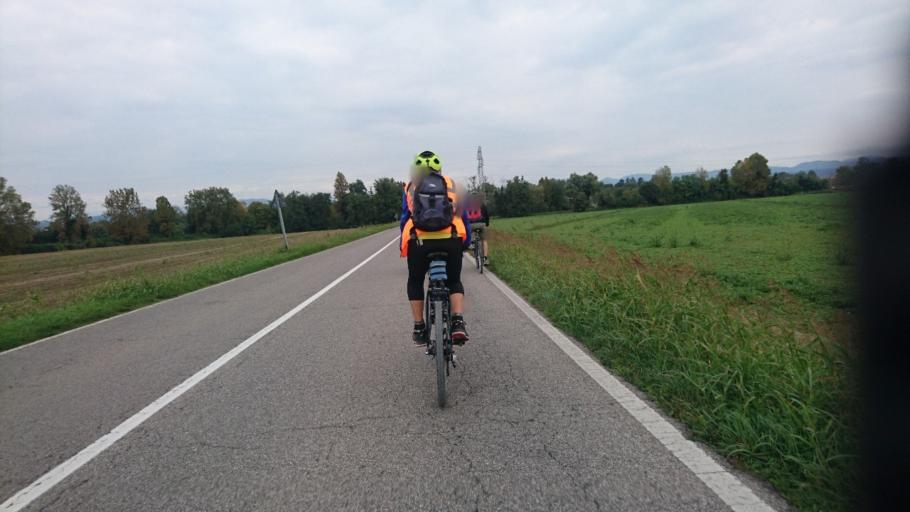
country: IT
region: Veneto
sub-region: Provincia di Verona
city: Zevio
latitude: 45.4003
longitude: 11.1250
